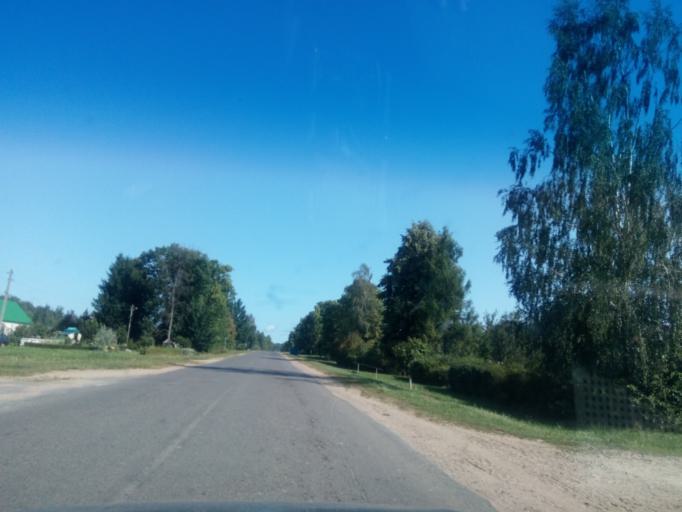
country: BY
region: Vitebsk
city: Dzisna
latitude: 55.6558
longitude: 28.3225
